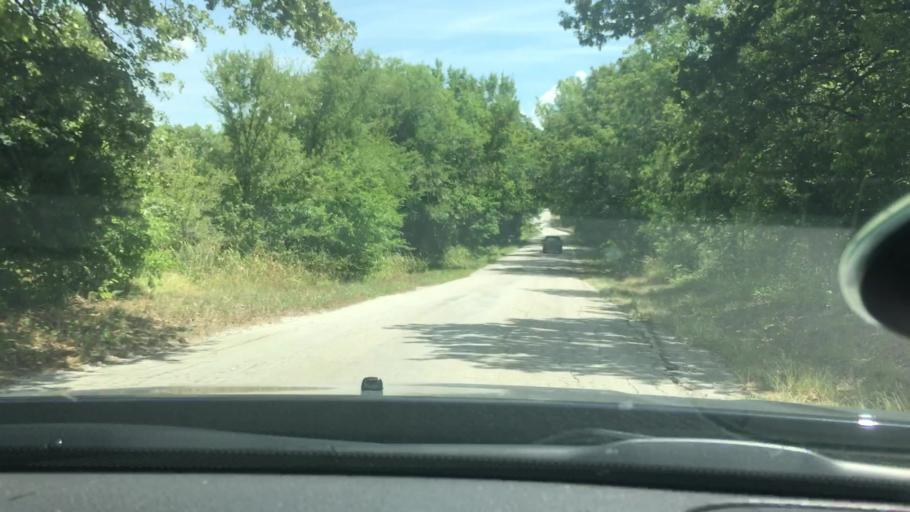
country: US
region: Oklahoma
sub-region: Carter County
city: Ardmore
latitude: 34.0739
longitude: -97.1812
